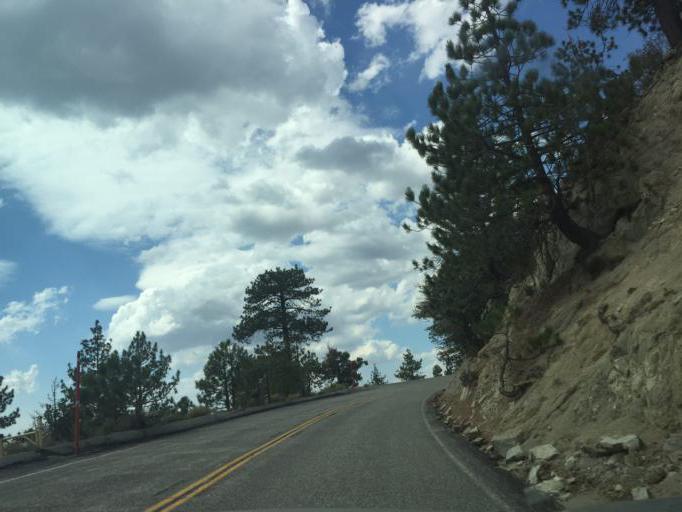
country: US
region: California
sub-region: Los Angeles County
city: Littlerock
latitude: 34.3521
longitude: -117.9455
